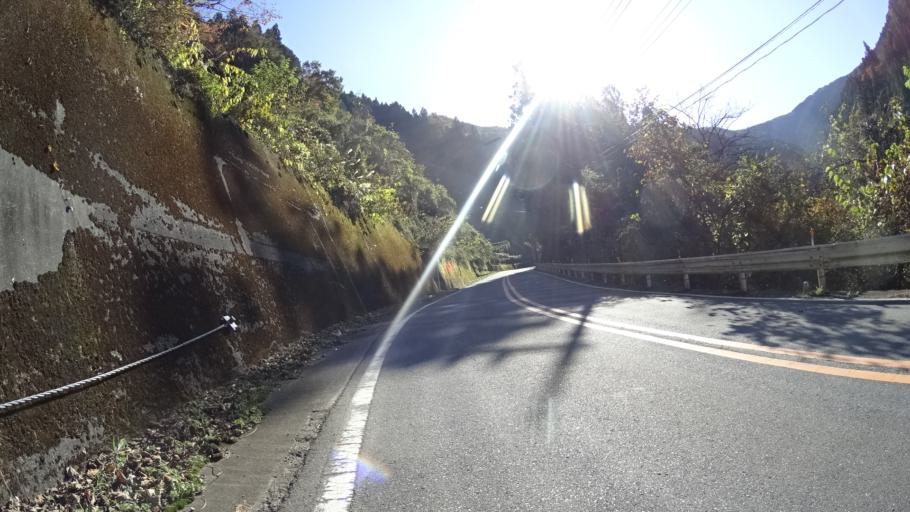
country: JP
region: Yamanashi
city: Uenohara
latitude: 35.6994
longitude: 139.1010
